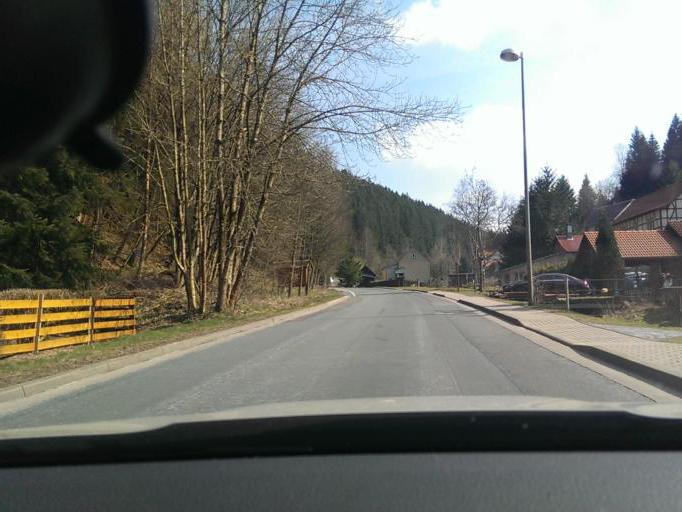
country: DE
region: Thuringia
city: Luisenthal
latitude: 50.7682
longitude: 10.7300
